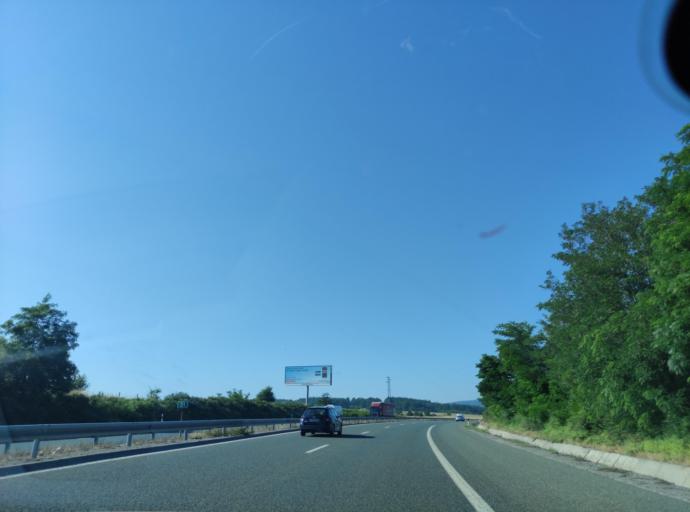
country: BG
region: Pernik
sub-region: Obshtina Pernik
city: Pernik
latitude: 42.5821
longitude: 23.1210
